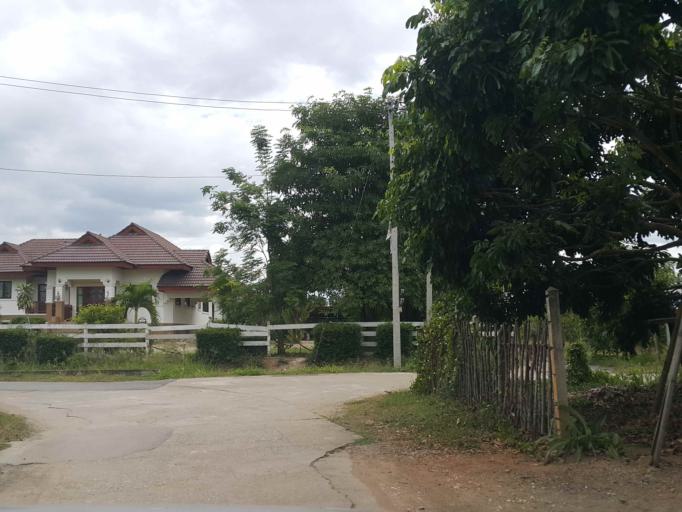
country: TH
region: Lamphun
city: Pa Sang
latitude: 18.4625
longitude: 98.9110
